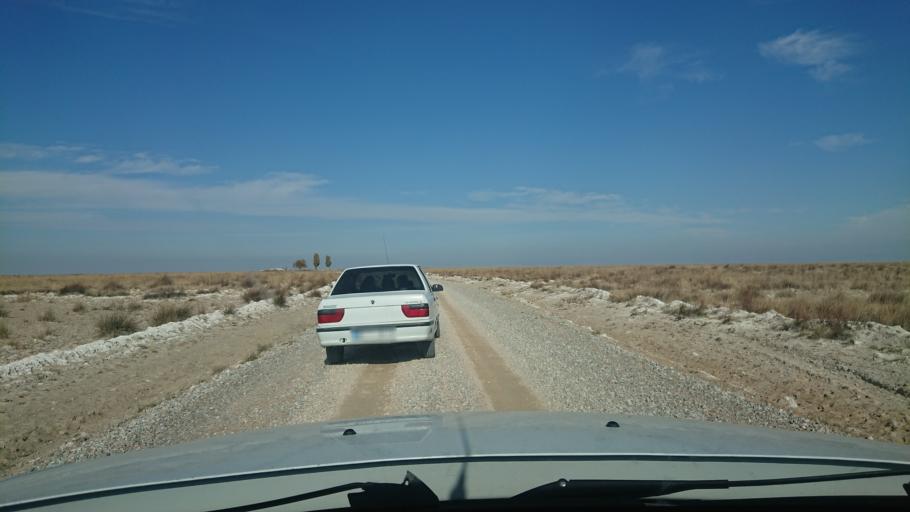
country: TR
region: Aksaray
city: Eskil
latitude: 38.4703
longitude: 33.4565
